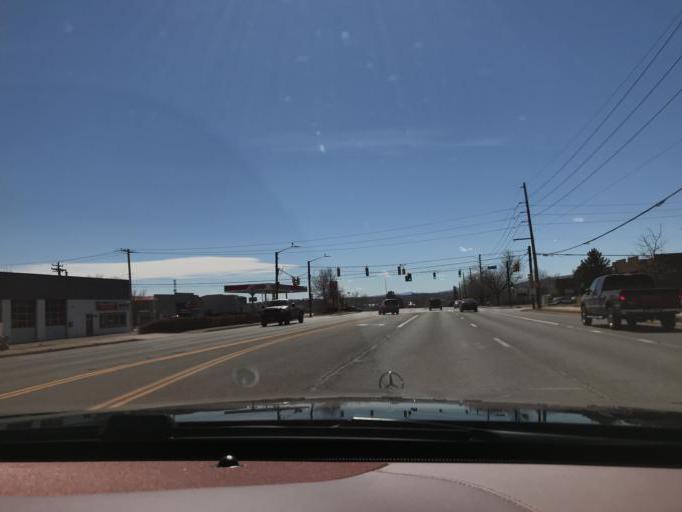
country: US
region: Colorado
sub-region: Jefferson County
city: Applewood
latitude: 39.7918
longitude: -105.1381
